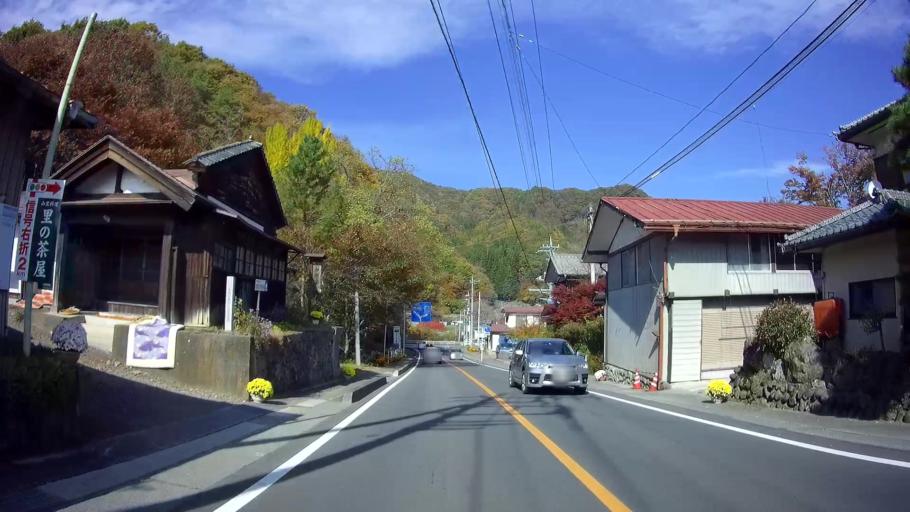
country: JP
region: Gunma
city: Nakanojomachi
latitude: 36.5121
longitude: 138.7748
